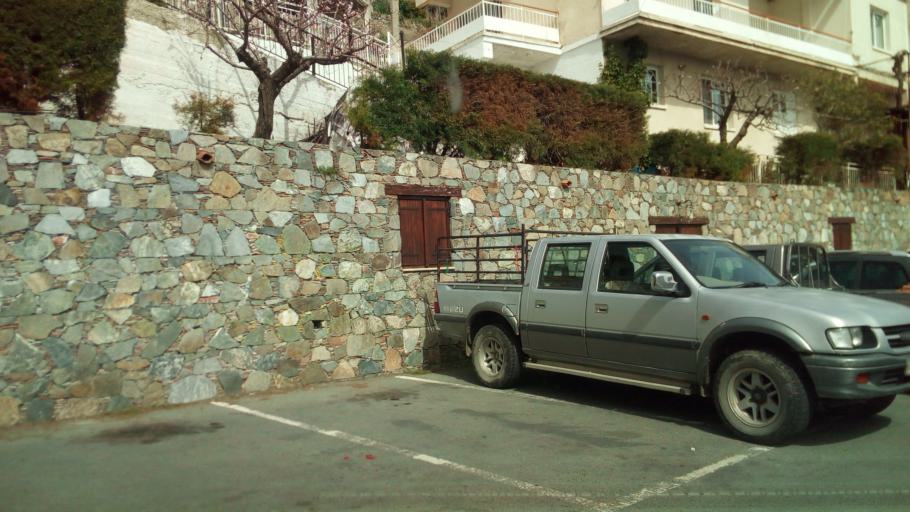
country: CY
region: Limassol
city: Pelendri
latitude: 34.8959
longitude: 32.9650
